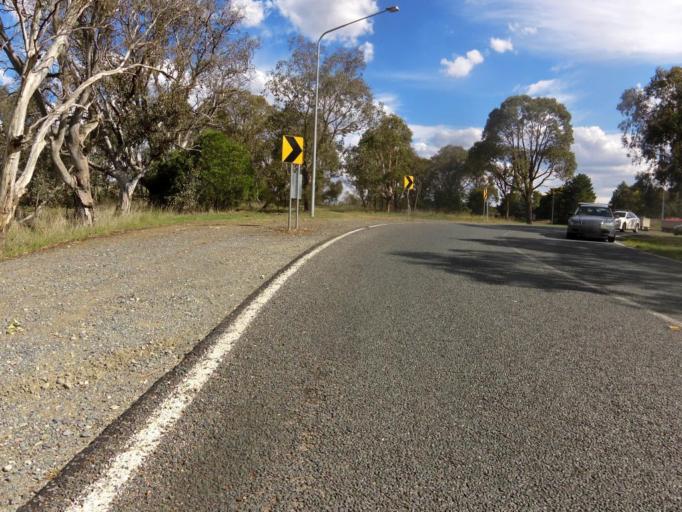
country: AU
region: Australian Capital Territory
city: Belconnen
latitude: -35.1803
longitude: 149.0737
